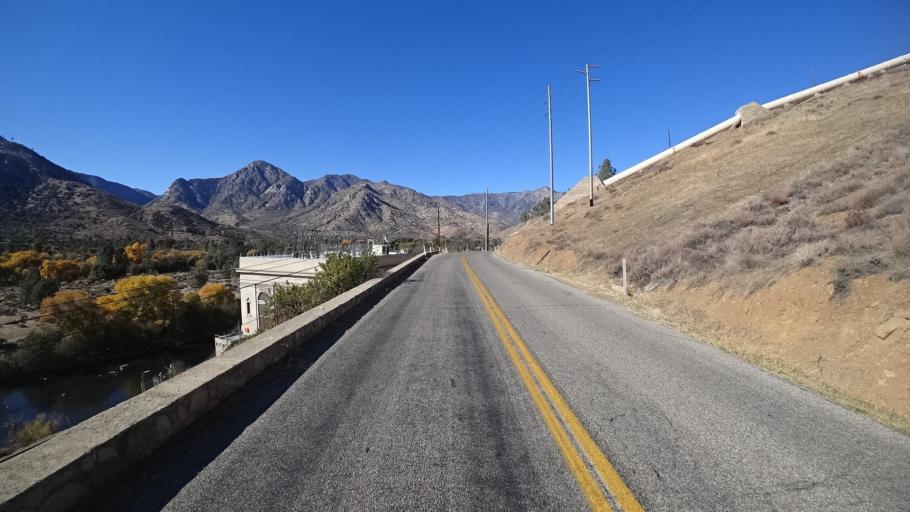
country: US
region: California
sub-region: Kern County
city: Kernville
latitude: 35.7759
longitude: -118.4353
